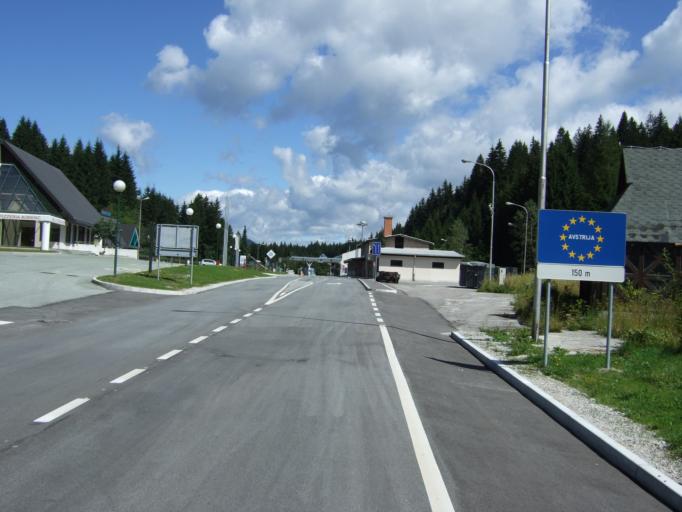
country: AT
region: Carinthia
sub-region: Politischer Bezirk Villach Land
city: Arnoldstein
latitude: 46.5161
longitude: 13.7513
